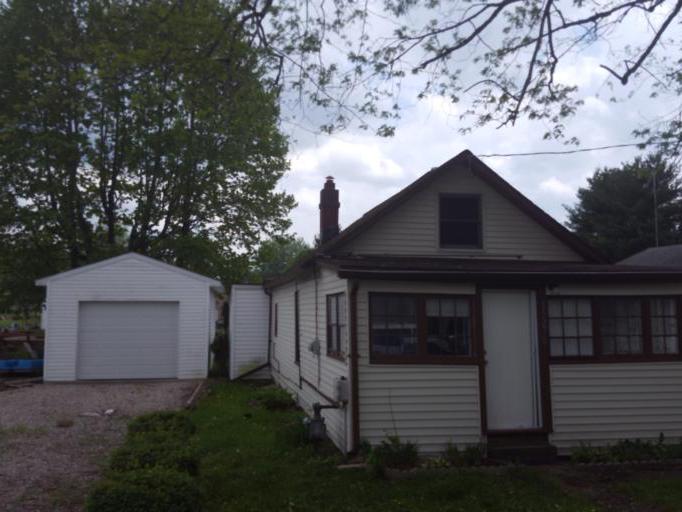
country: US
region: Ohio
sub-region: Licking County
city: Harbor Hills
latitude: 39.9230
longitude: -82.4328
